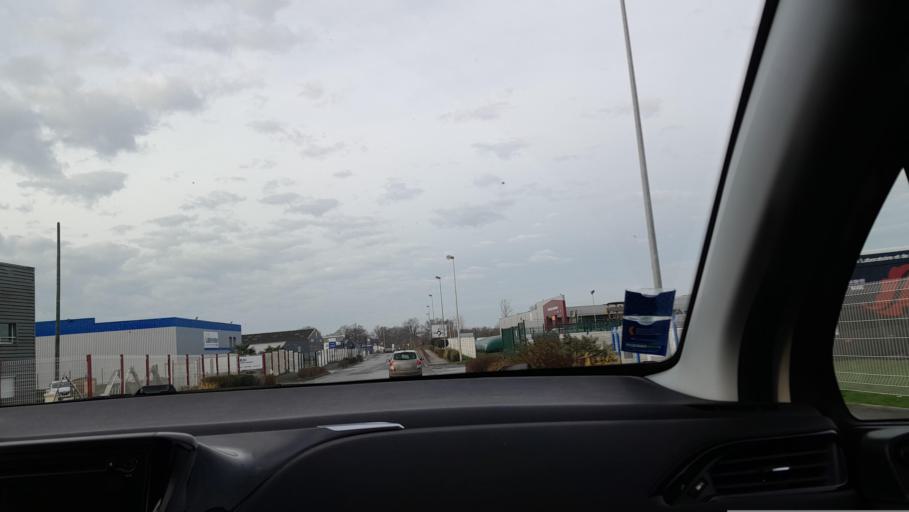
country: FR
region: Brittany
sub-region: Departement d'Ille-et-Vilaine
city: La Guerche-de-Bretagne
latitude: 47.9337
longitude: -1.2292
